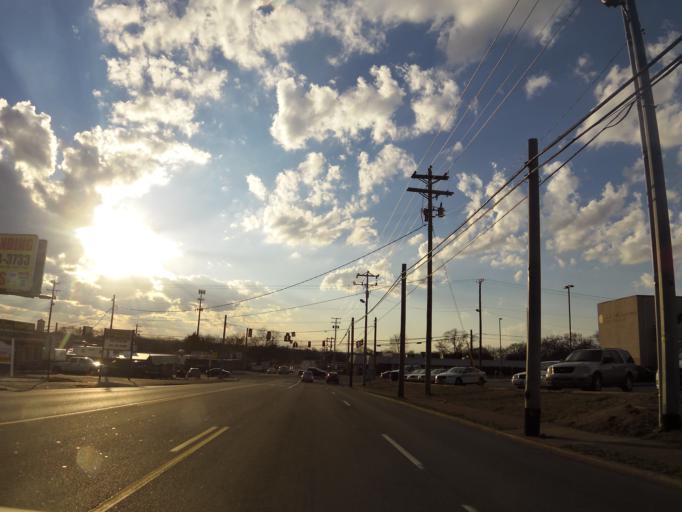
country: US
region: Tennessee
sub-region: Wilson County
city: Lebanon
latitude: 36.2124
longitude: -86.2893
